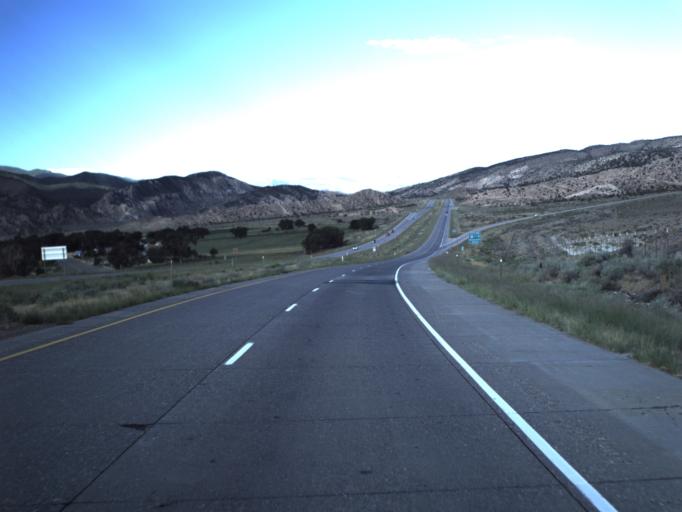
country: US
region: Utah
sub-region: Sevier County
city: Monroe
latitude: 38.6040
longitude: -112.2385
